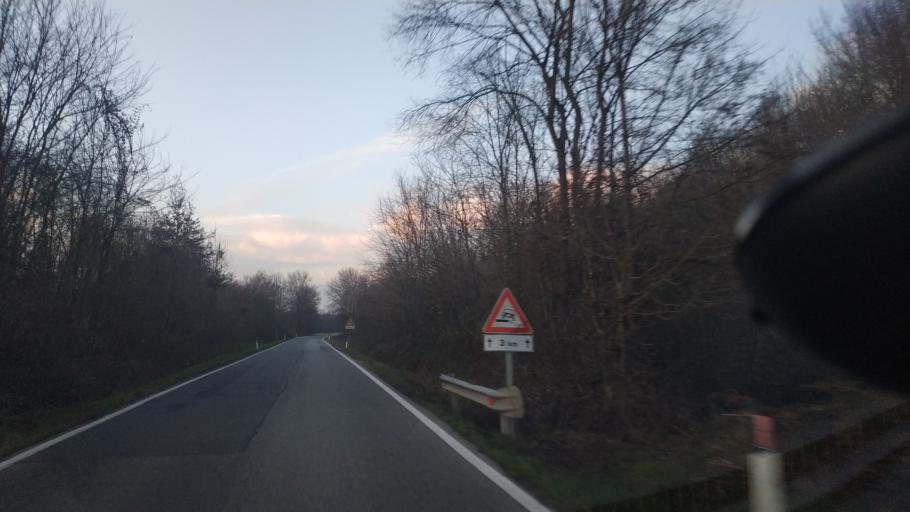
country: IT
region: Piedmont
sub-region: Provincia di Torino
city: Montanaro
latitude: 45.2489
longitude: 7.8398
